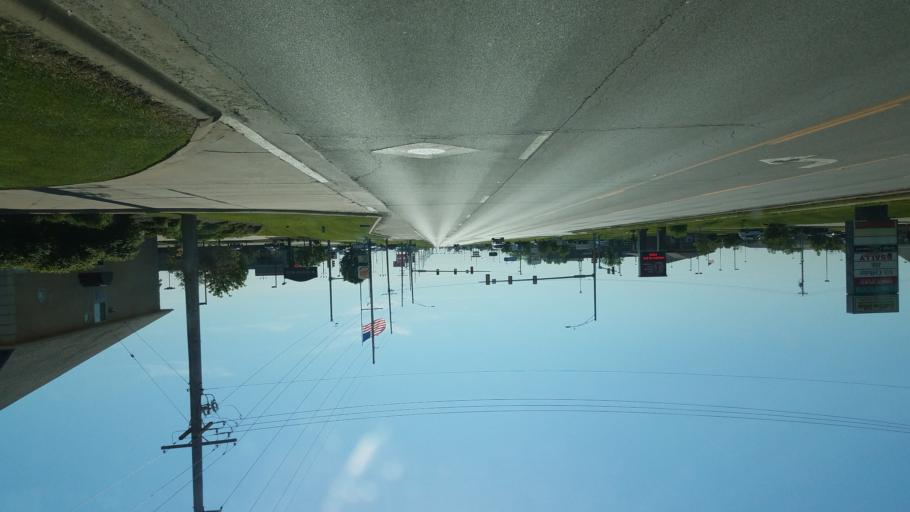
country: US
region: Illinois
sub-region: McDonough County
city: Macomb
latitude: 40.4585
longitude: -90.6455
